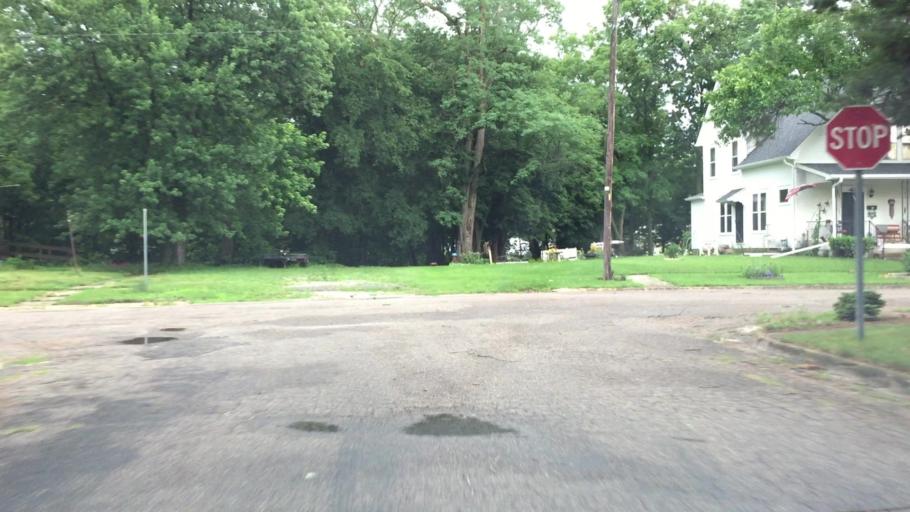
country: US
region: Illinois
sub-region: Hancock County
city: Warsaw
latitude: 40.3620
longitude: -91.4375
